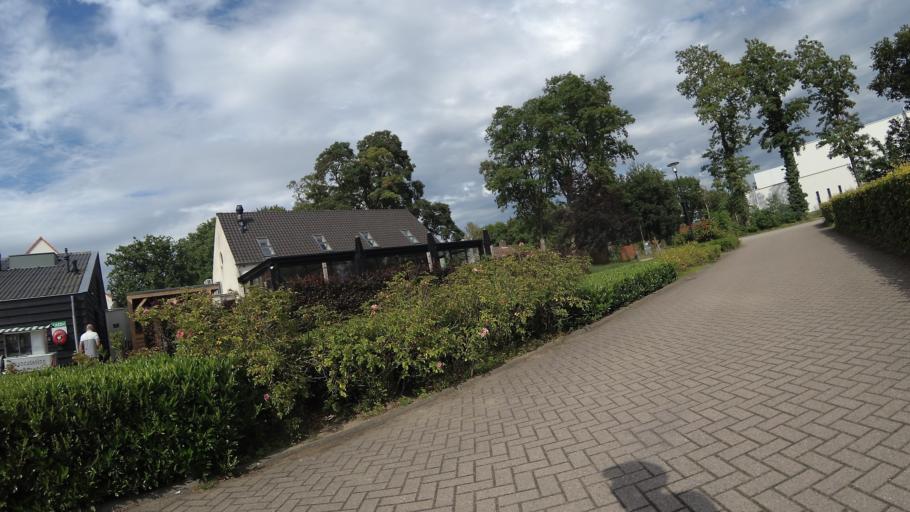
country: NL
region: North Brabant
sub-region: Gemeente Breda
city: Hoge Vucht
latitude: 51.6353
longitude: 4.7948
